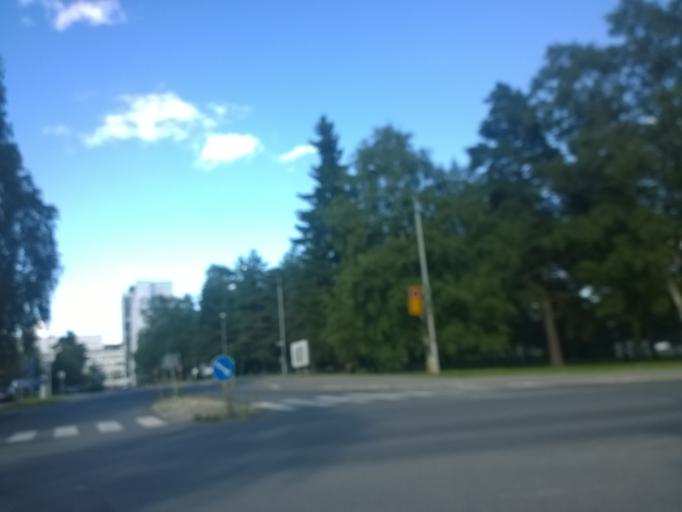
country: FI
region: Pirkanmaa
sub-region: Tampere
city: Tampere
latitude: 61.5032
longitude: 23.8115
